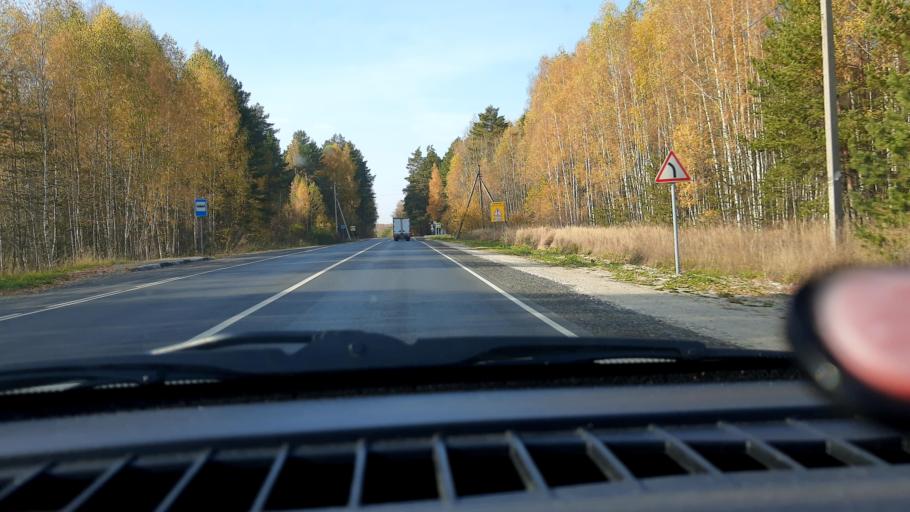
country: RU
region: Nizjnij Novgorod
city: Novaya Balakhna
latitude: 56.6133
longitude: 43.5913
